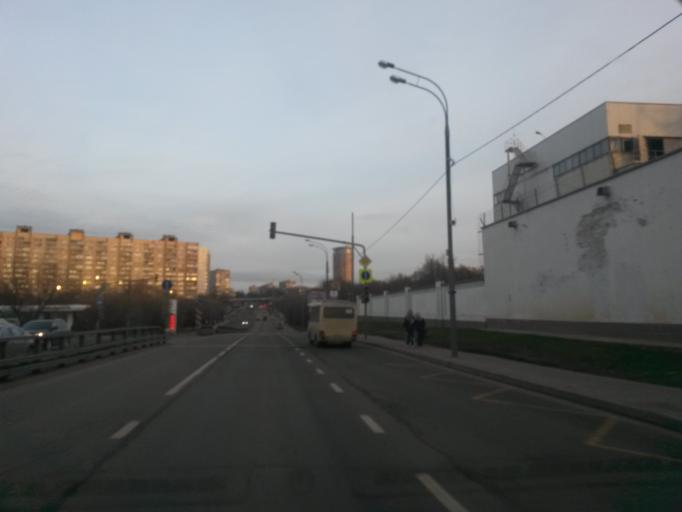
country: RU
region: Moskovskaya
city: Bol'shaya Setun'
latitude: 55.7139
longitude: 37.4231
